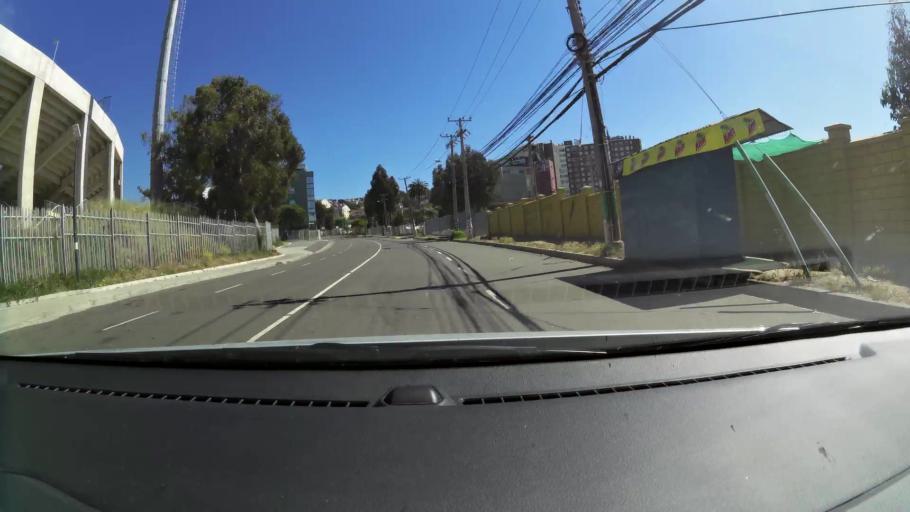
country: CL
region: Valparaiso
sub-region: Provincia de Valparaiso
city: Valparaiso
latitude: -33.0223
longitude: -71.6410
